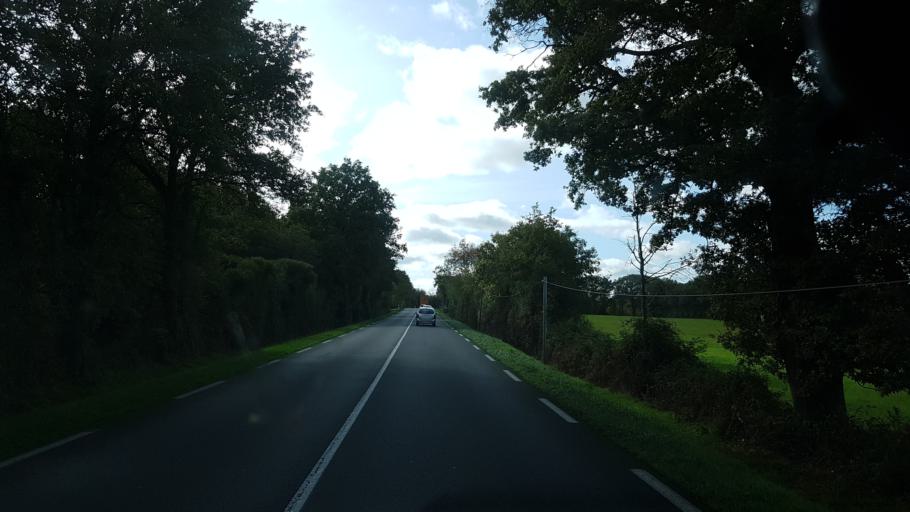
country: FR
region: Poitou-Charentes
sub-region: Departement de la Charente
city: Confolens
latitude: 46.0641
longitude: 0.7102
